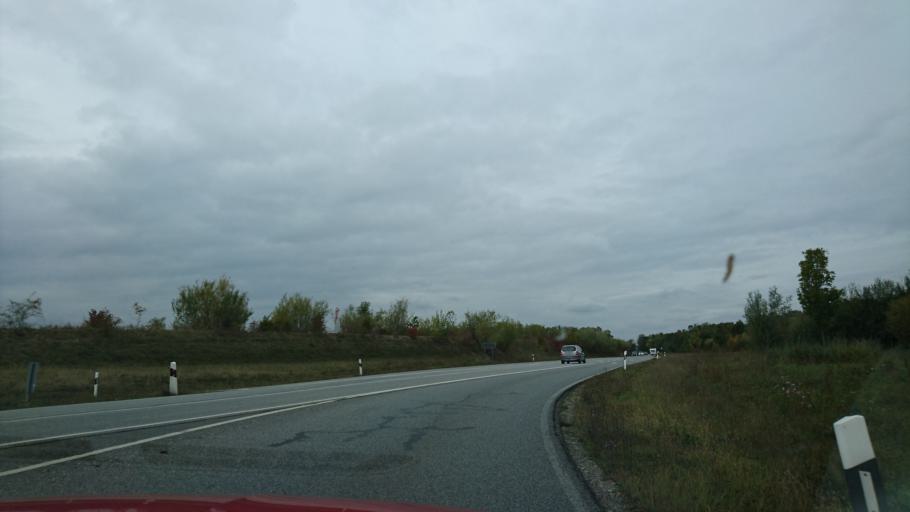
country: DE
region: Bavaria
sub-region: Upper Bavaria
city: Aschheim
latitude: 48.1750
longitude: 11.7309
